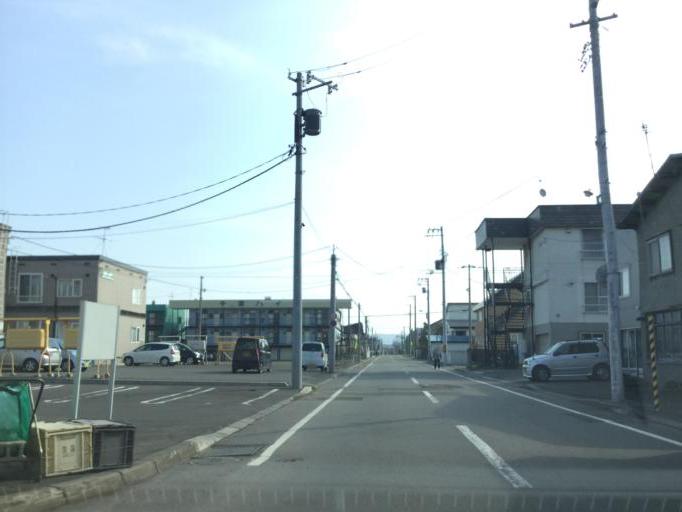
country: JP
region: Hokkaido
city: Iwamizawa
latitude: 43.2066
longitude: 141.7667
